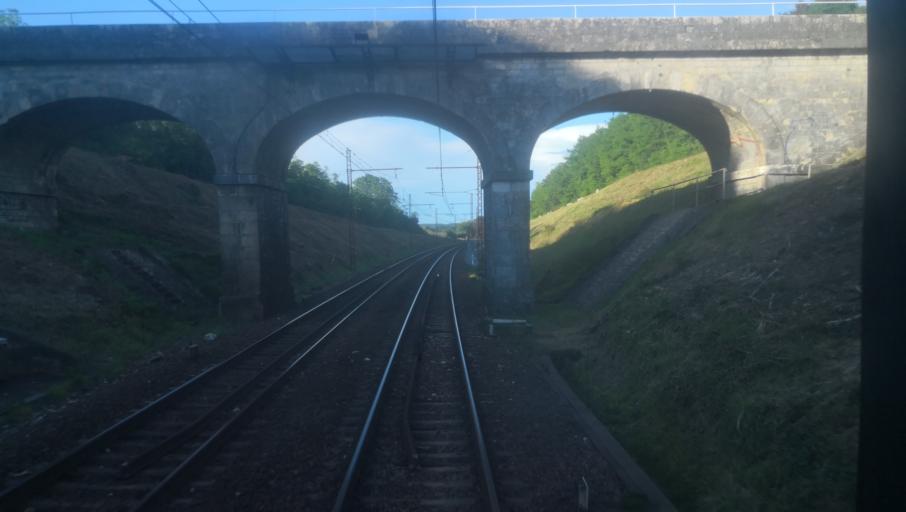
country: FR
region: Centre
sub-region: Departement du Cher
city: Vierzon
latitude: 47.1895
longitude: 2.0720
